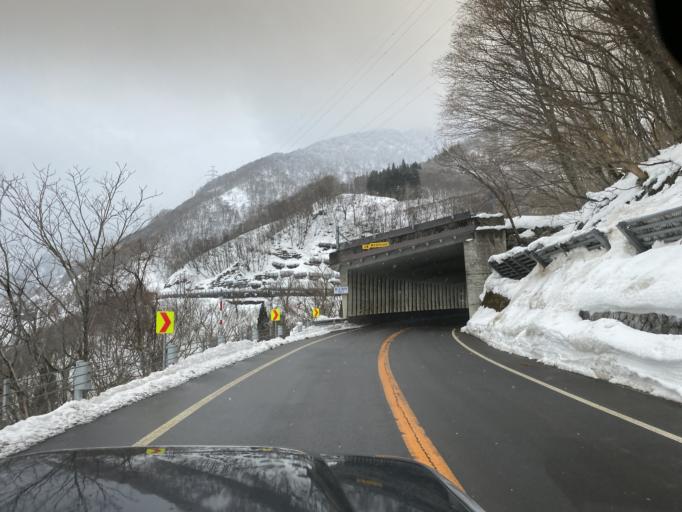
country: JP
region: Gifu
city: Takayama
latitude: 36.1449
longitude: 136.9074
